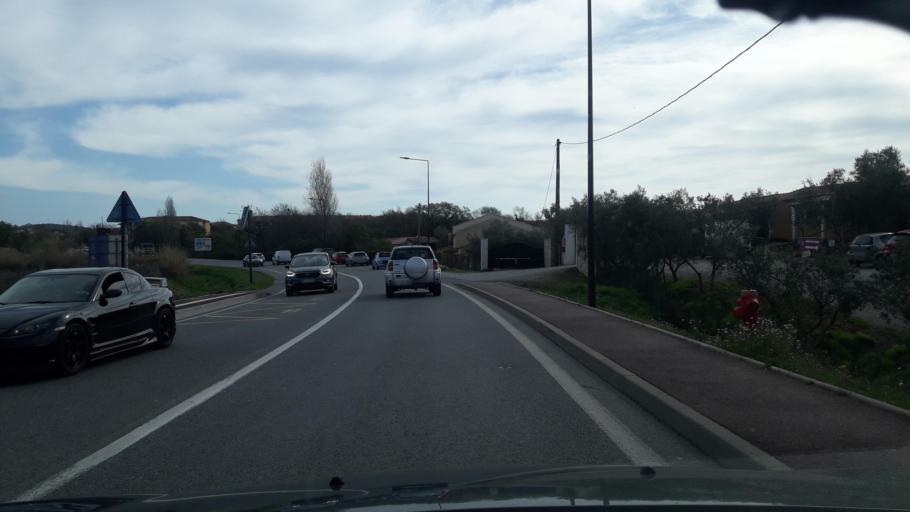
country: FR
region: Provence-Alpes-Cote d'Azur
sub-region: Departement du Var
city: Saint-Raphael
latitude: 43.4362
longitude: 6.7593
